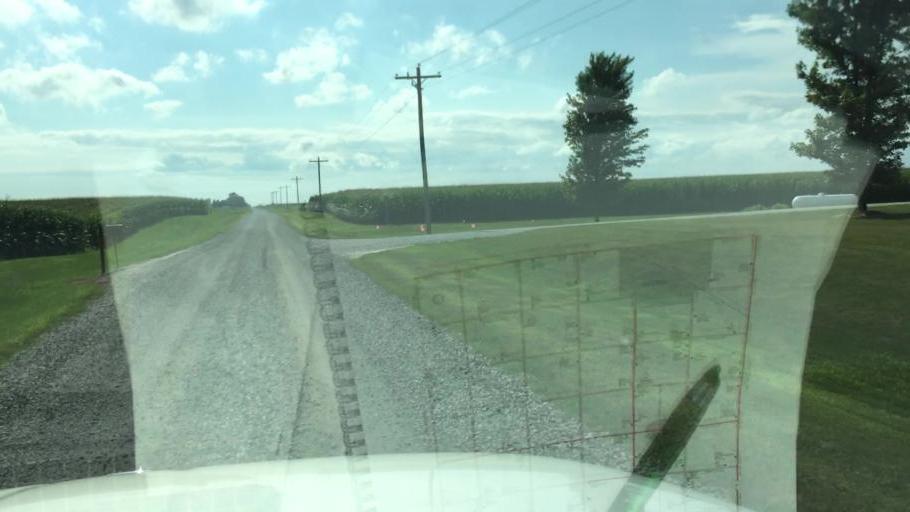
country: US
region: Illinois
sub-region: Hancock County
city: Nauvoo
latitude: 40.5213
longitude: -91.2770
